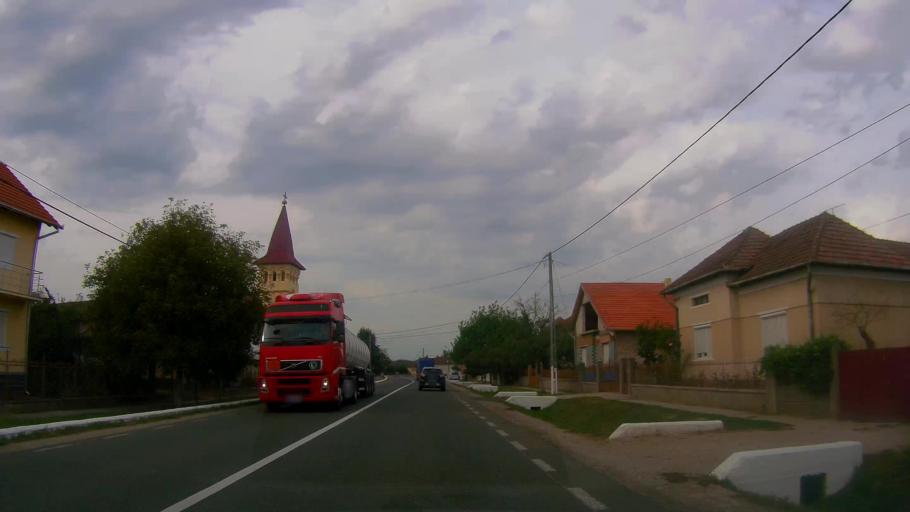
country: RO
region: Satu Mare
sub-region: Comuna Beltiug
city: Beltiug
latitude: 47.5475
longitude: 22.8394
